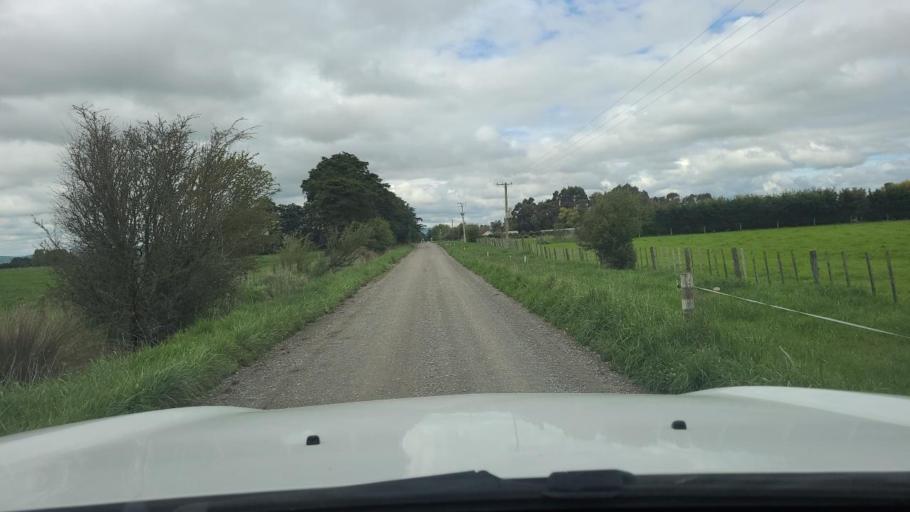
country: NZ
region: Wellington
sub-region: South Wairarapa District
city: Waipawa
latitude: -41.1441
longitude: 175.3757
